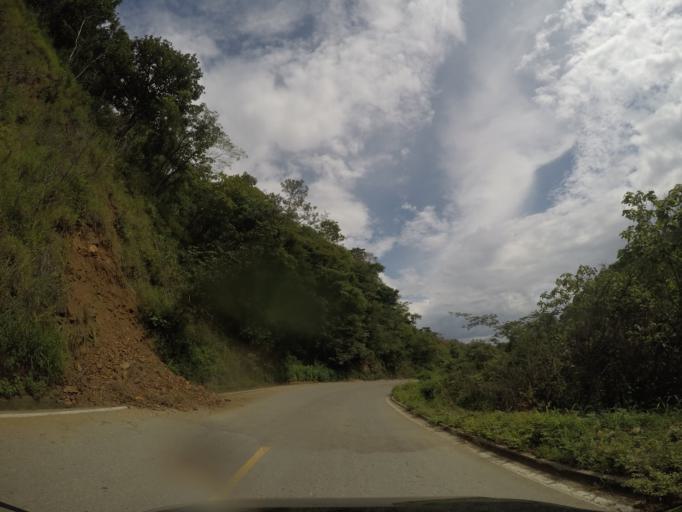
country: MX
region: Oaxaca
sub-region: San Jeronimo Coatlan
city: San Cristobal Honduras
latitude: 16.3863
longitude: -97.0759
